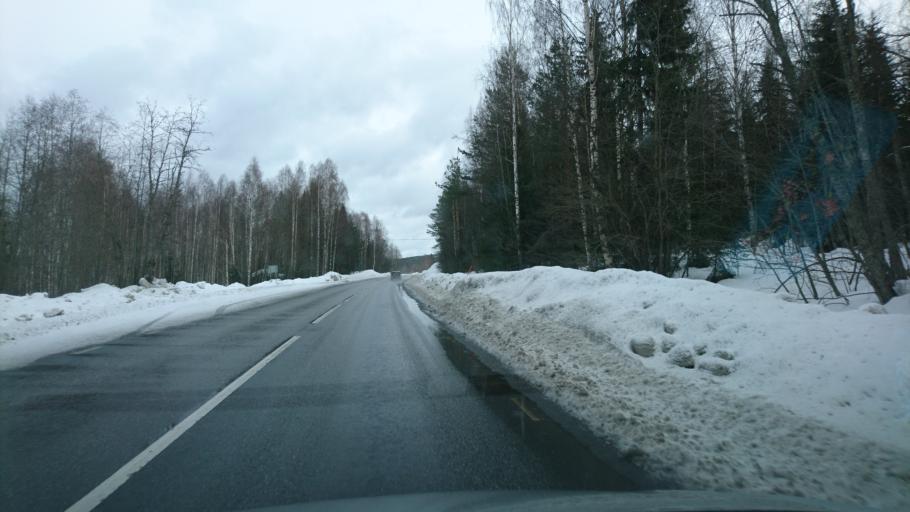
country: SE
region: Vaesternorrland
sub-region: Solleftea Kommun
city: Solleftea
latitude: 63.1499
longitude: 16.9846
